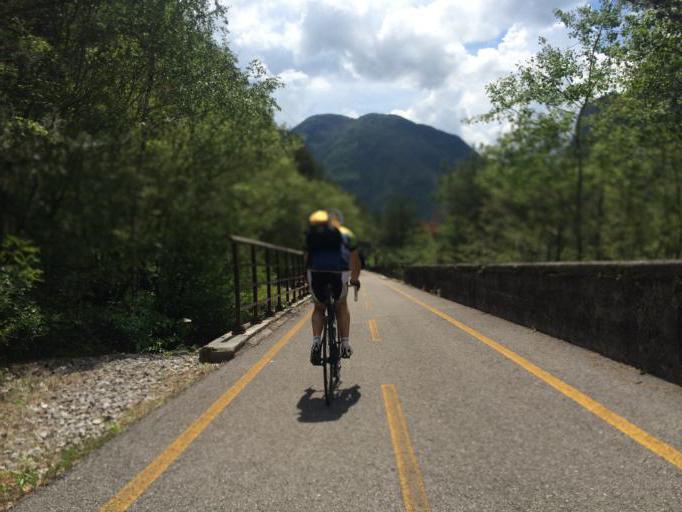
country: IT
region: Friuli Venezia Giulia
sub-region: Provincia di Udine
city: Dogna
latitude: 46.4319
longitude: 13.3153
